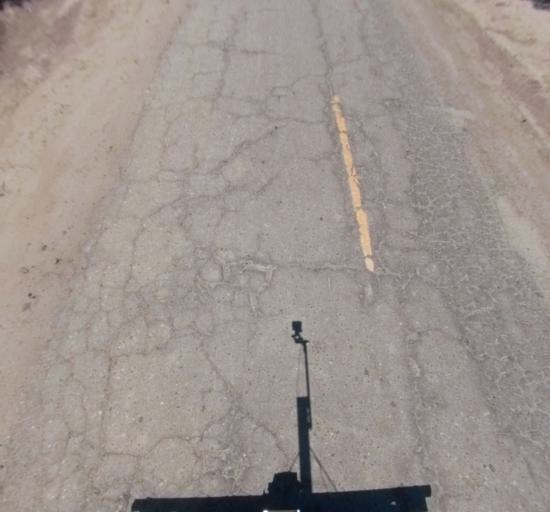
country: US
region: California
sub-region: Madera County
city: Chowchilla
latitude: 37.0796
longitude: -120.2659
